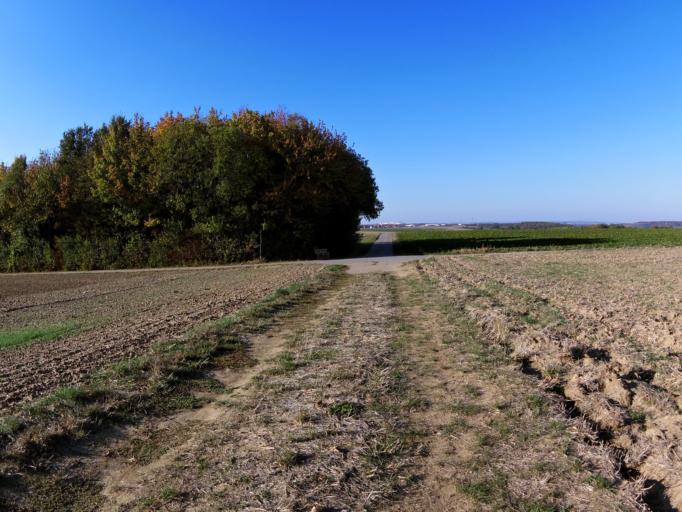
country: DE
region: Bavaria
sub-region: Regierungsbezirk Unterfranken
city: Eibelstadt
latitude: 49.7068
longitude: 9.9838
